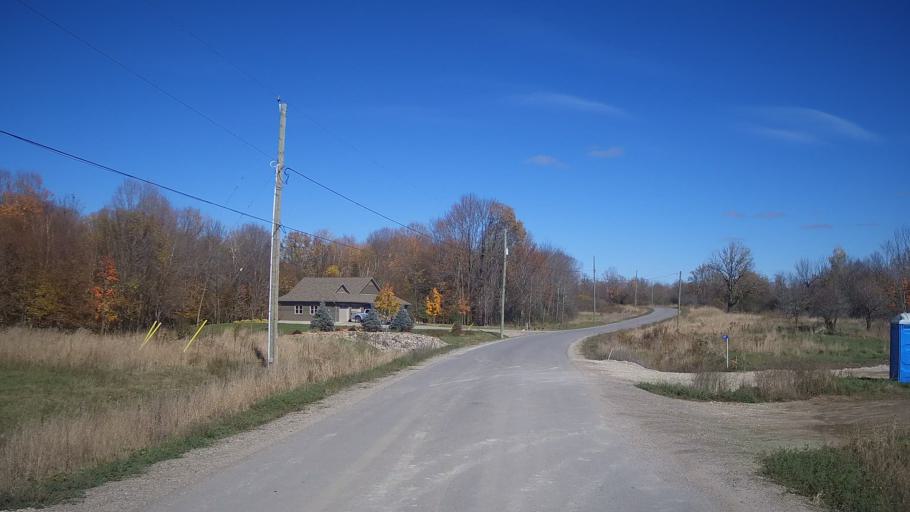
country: CA
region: Ontario
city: Perth
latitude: 44.8799
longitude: -76.2959
